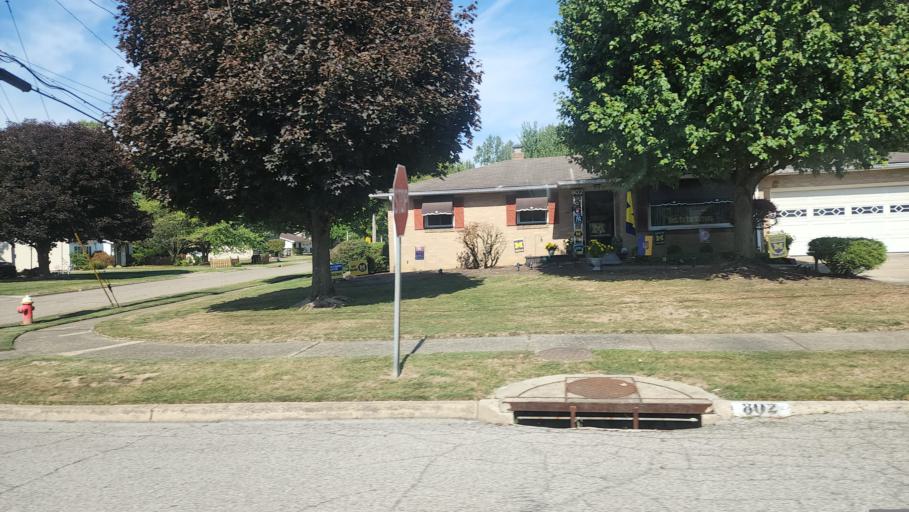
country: US
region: Ohio
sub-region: Trumbull County
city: Niles
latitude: 41.1916
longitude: -80.7563
